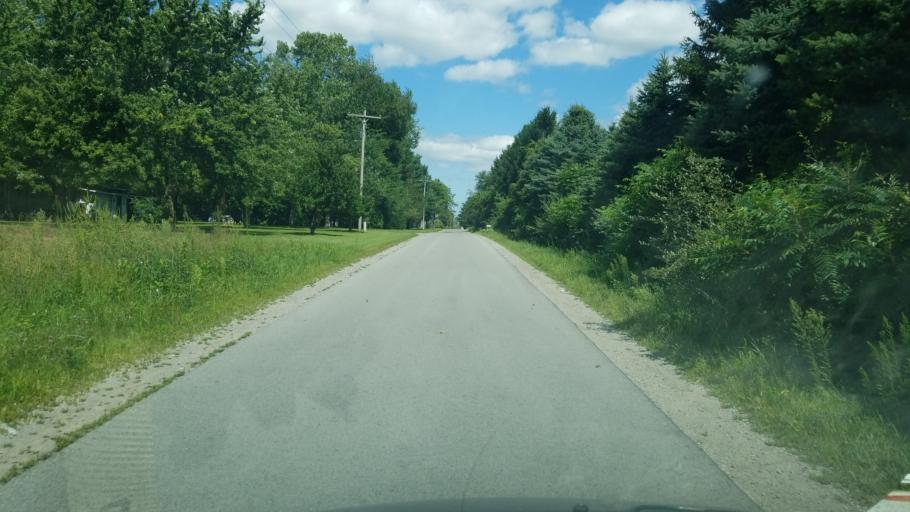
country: US
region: Ohio
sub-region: Henry County
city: Liberty Center
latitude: 41.4634
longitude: -83.9412
